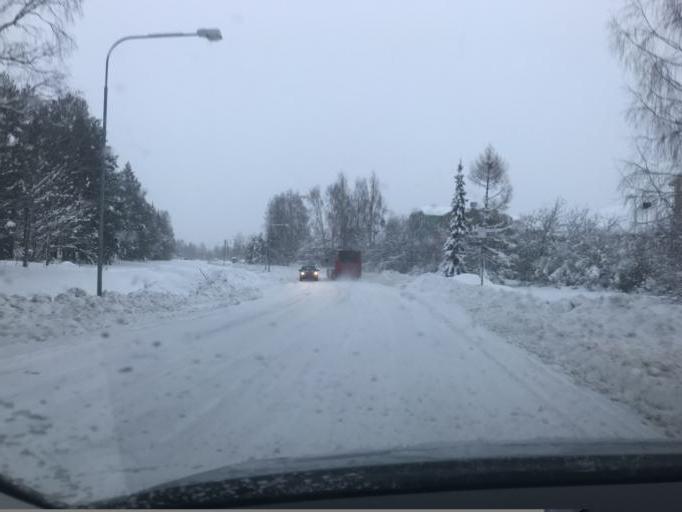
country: SE
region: Norrbotten
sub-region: Lulea Kommun
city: Bergnaset
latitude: 65.6183
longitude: 22.1225
